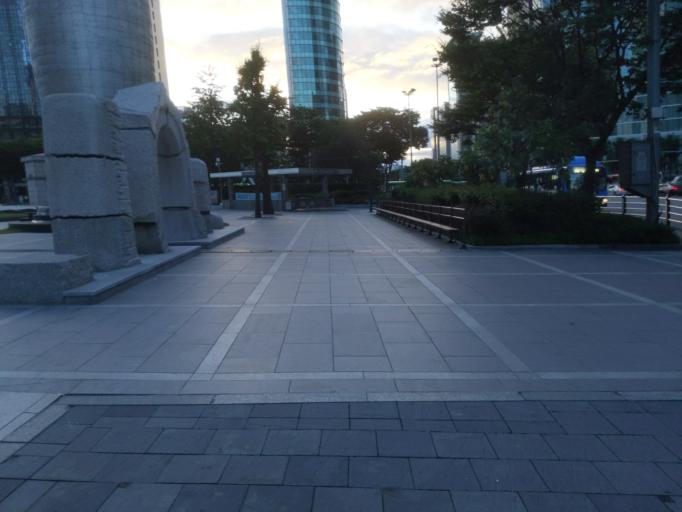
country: KR
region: Seoul
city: Seoul
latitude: 37.5086
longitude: 127.0620
